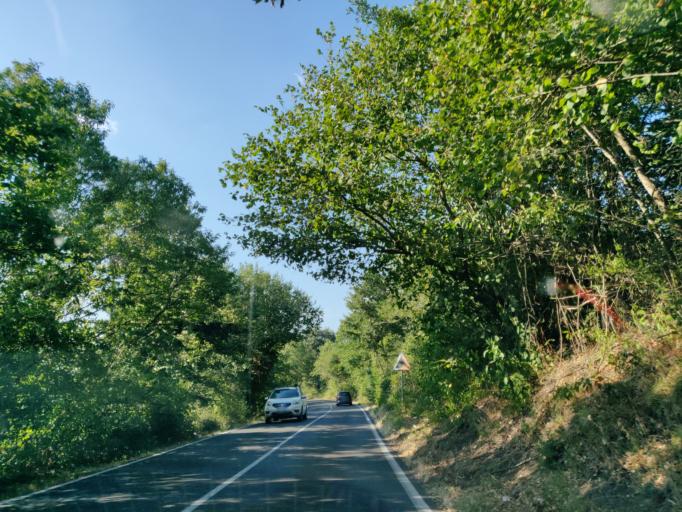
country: IT
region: Latium
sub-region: Provincia di Viterbo
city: Latera
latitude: 42.6279
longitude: 11.8370
